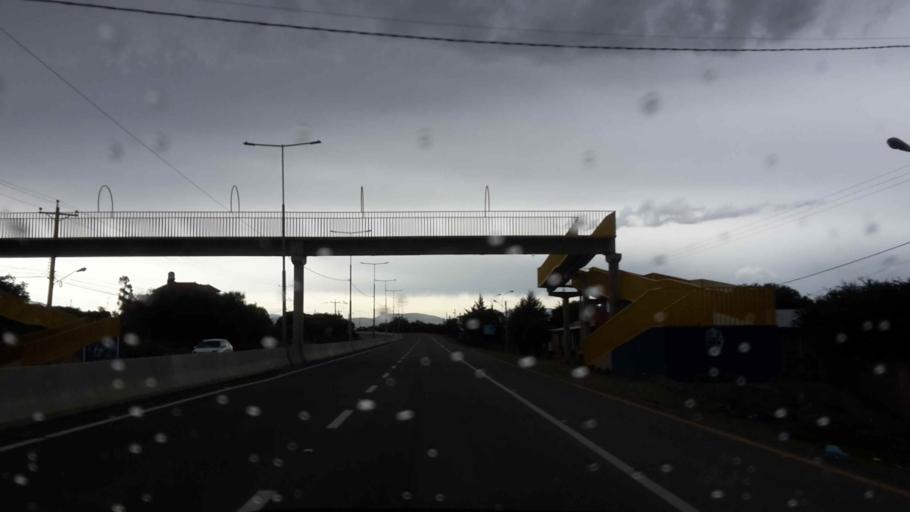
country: BO
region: Cochabamba
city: Tarata
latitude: -17.5453
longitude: -66.0160
